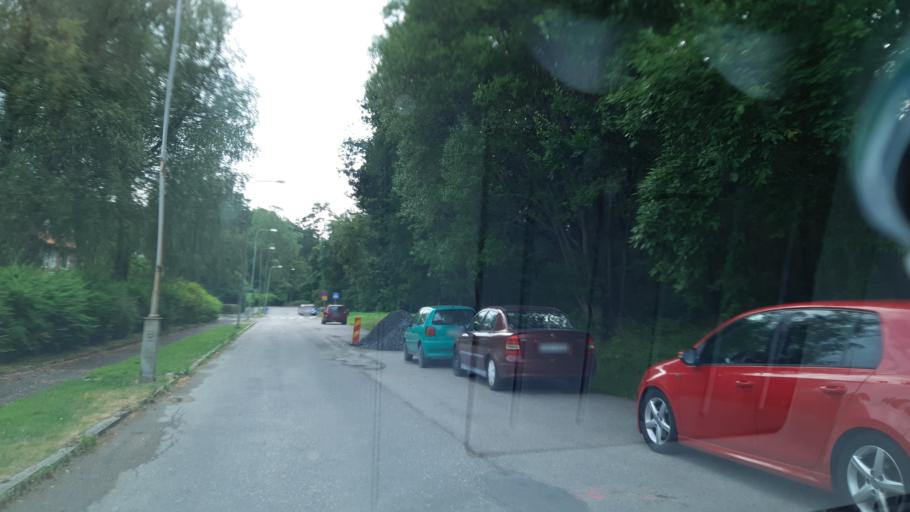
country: SE
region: Vaestra Goetaland
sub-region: Partille Kommun
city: Partille
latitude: 57.7145
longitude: 12.0593
